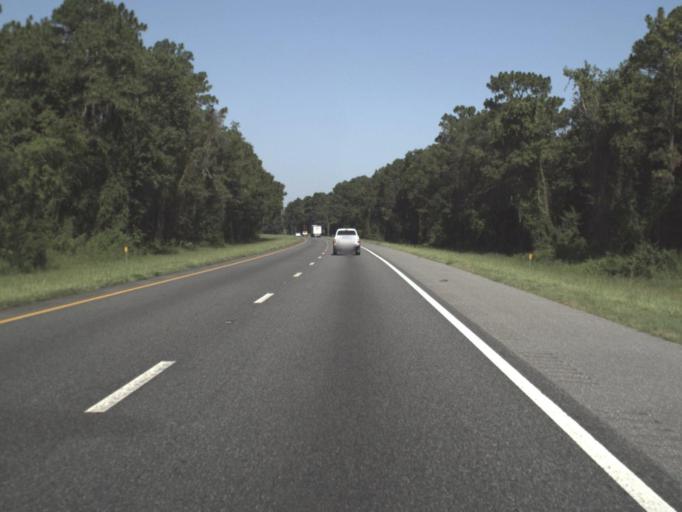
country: US
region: Florida
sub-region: Suwannee County
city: Wellborn
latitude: 30.2856
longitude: -82.8349
